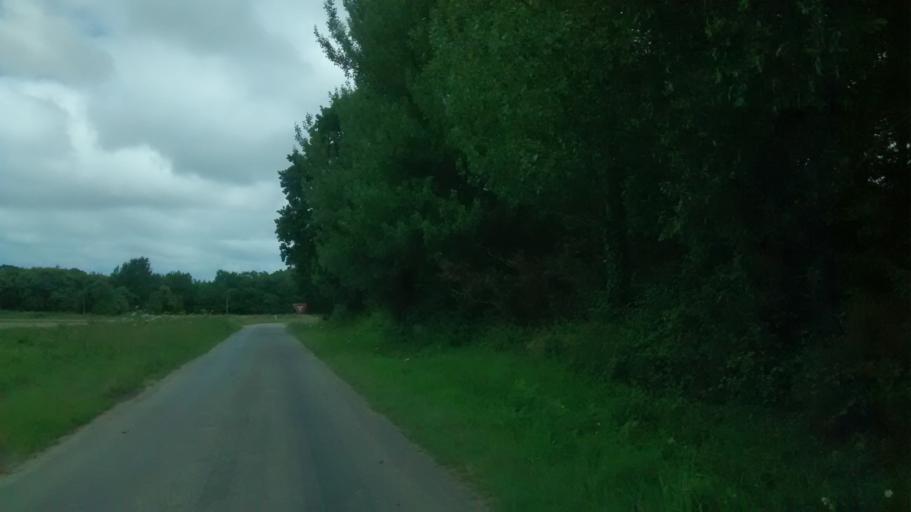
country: FR
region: Brittany
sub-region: Departement d'Ille-et-Vilaine
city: Saint-Meloir-des-Ondes
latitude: 48.6479
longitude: -1.9101
